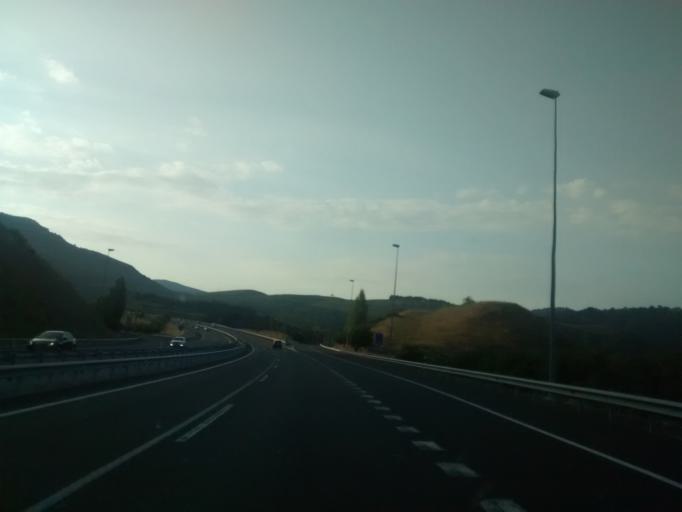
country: ES
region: Cantabria
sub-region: Provincia de Cantabria
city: Arenas de Iguna
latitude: 43.1814
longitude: -4.0574
